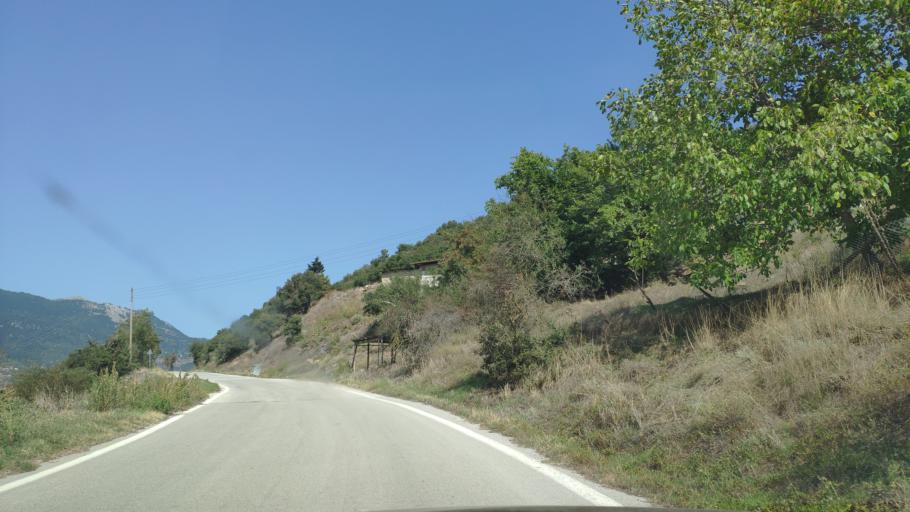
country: GR
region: West Greece
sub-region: Nomos Achaias
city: Aiyira
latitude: 37.9162
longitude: 22.3311
